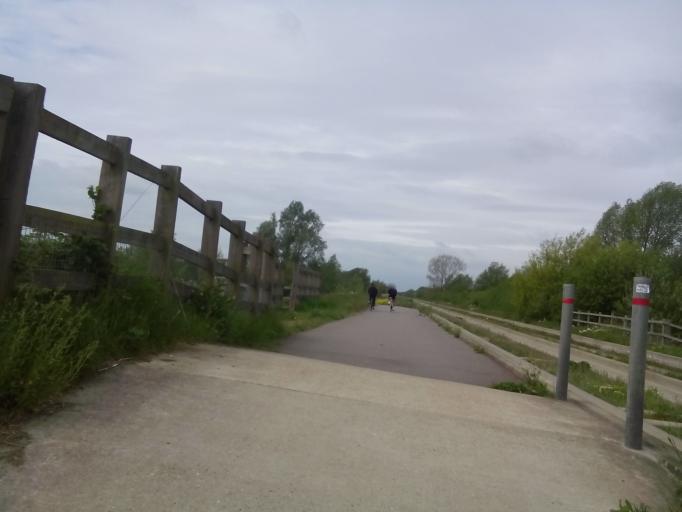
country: GB
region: England
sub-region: Cambridgeshire
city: Swavesey
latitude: 52.3073
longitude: -0.0173
